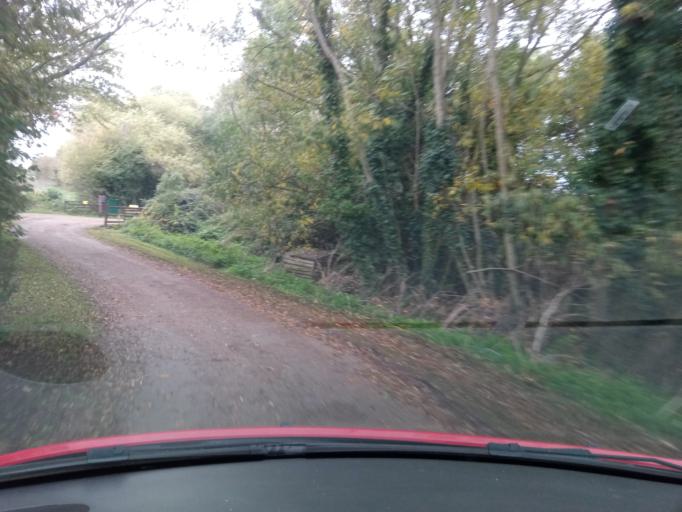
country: GB
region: England
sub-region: Essex
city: Brightlingsea
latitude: 51.7931
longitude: 0.9925
